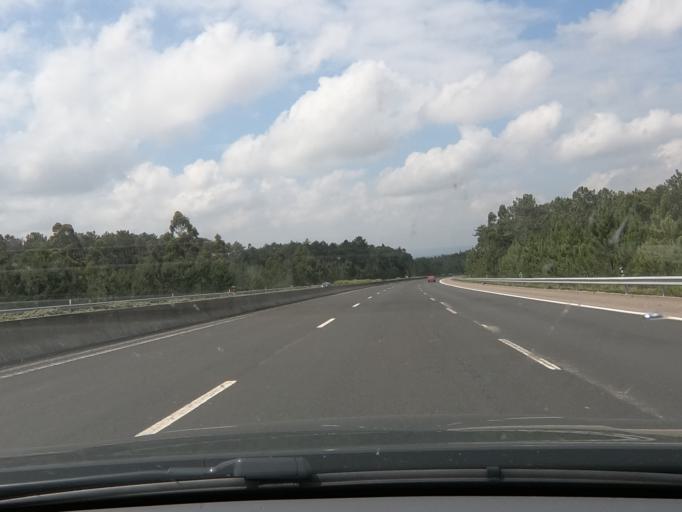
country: PT
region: Leiria
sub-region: Leiria
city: Maceira
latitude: 39.6828
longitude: -8.9363
